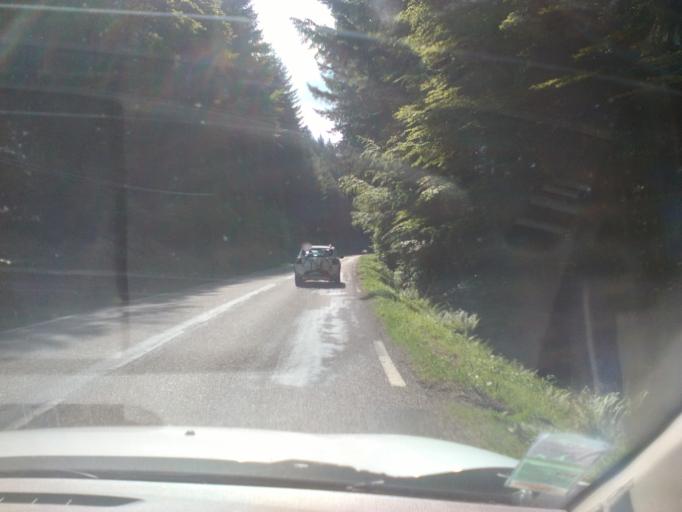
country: FR
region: Lorraine
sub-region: Departement des Vosges
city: Le Tholy
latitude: 48.1086
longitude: 6.6864
